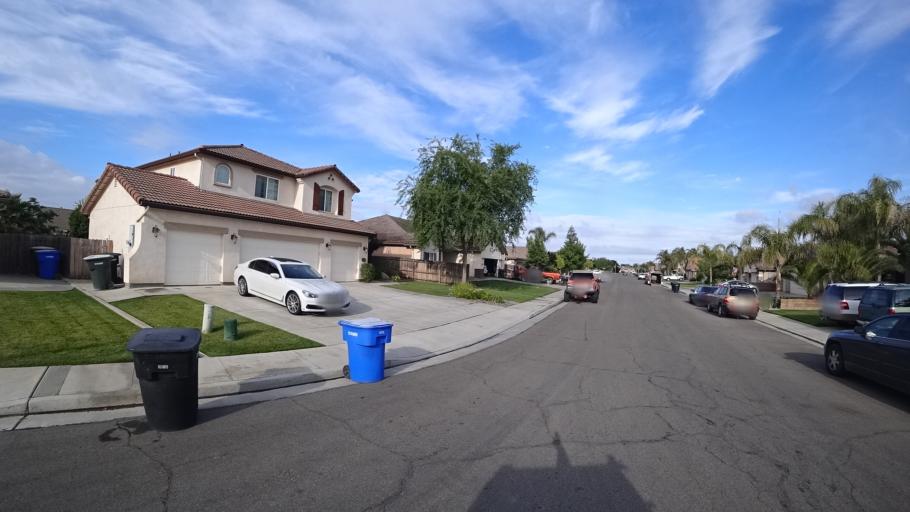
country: US
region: California
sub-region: Kings County
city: Lucerne
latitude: 36.3486
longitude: -119.6746
